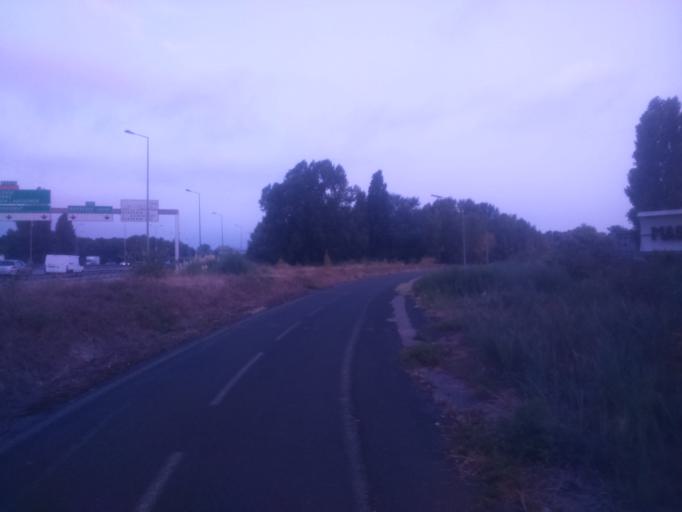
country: FR
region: Aquitaine
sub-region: Departement de la Gironde
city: Lormont
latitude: 44.8839
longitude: -0.5566
